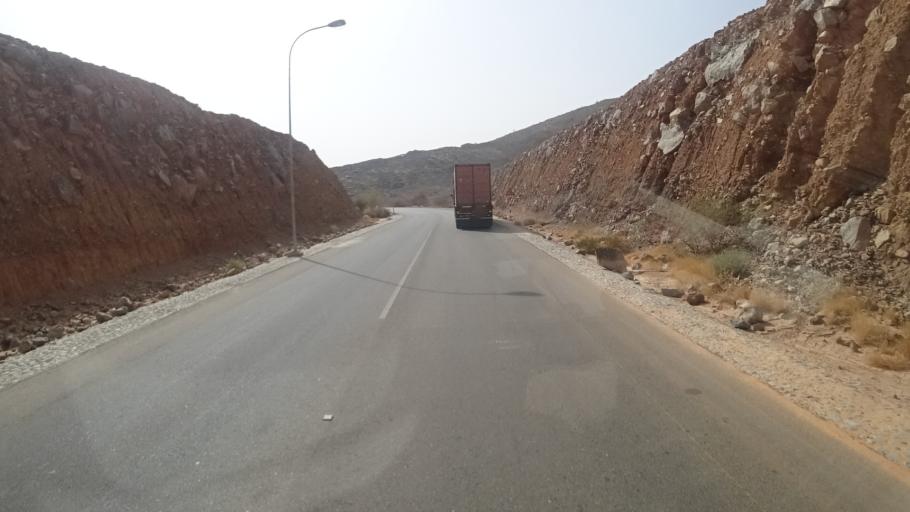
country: OM
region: Muhafazat ad Dakhiliyah
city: Nizwa
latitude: 23.0020
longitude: 57.5548
